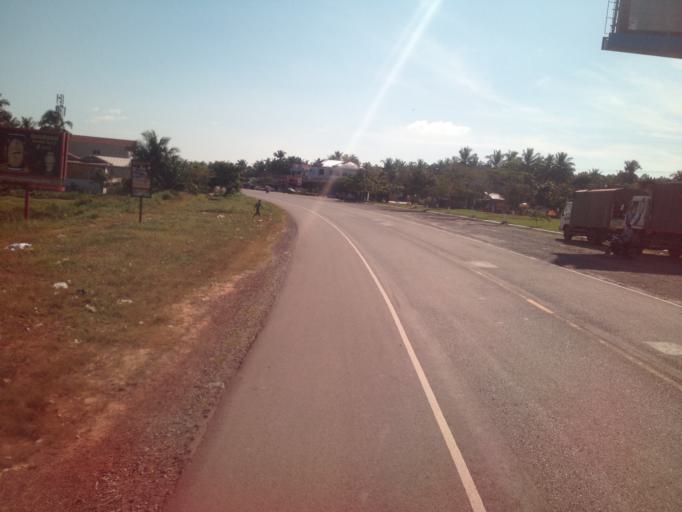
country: KH
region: Preah Sihanouk
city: Sihanoukville
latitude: 10.5857
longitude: 103.6445
